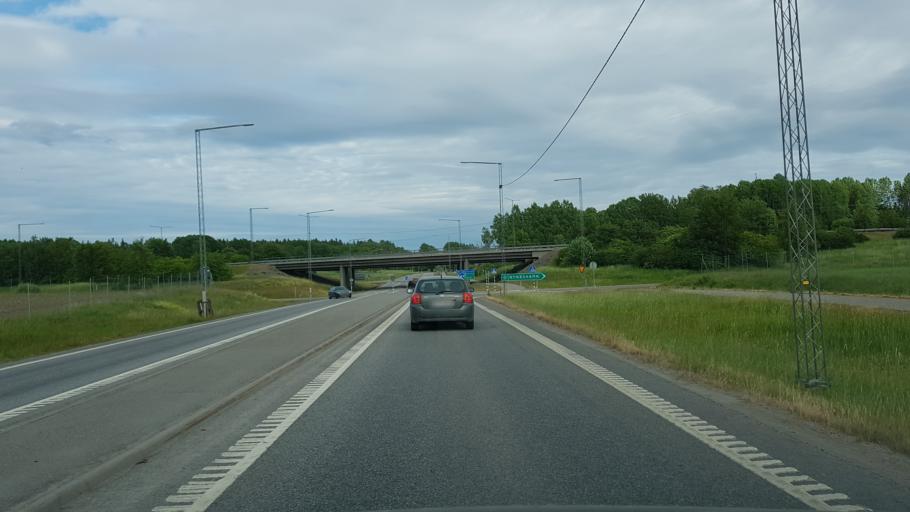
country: SE
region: Stockholm
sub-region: Haninge Kommun
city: Jordbro
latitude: 59.1221
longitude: 18.1294
